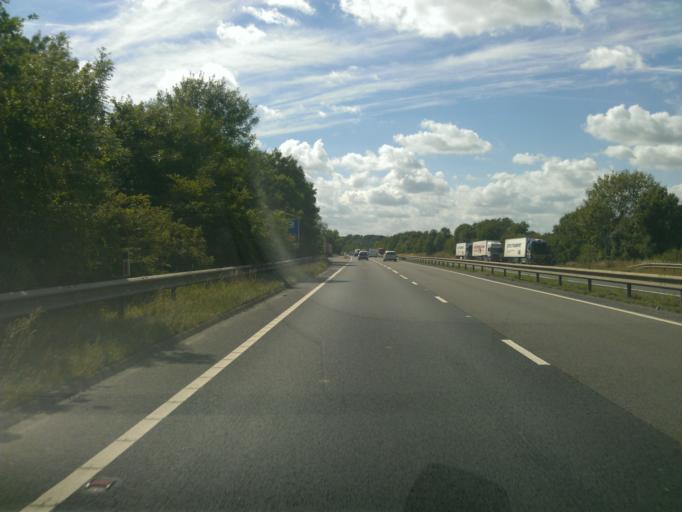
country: GB
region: England
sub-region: Northamptonshire
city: Thrapston
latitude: 52.3927
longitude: -0.5825
